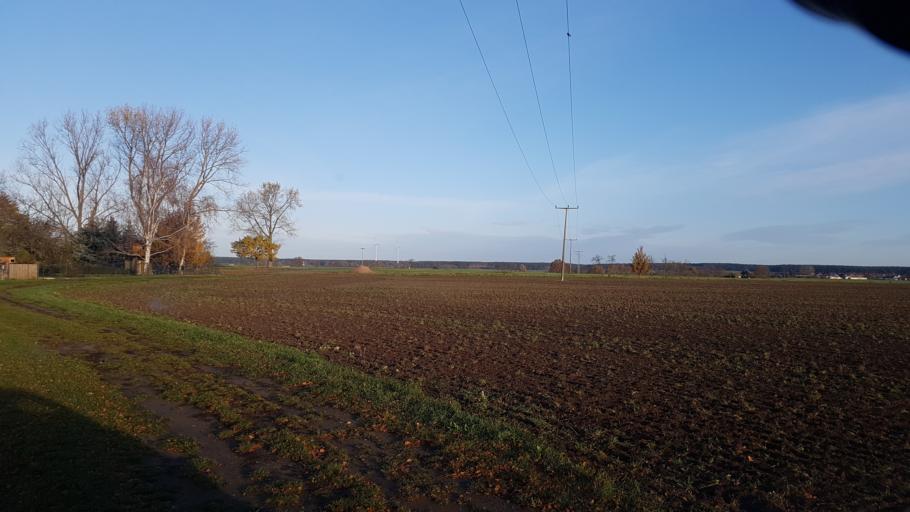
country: DE
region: Brandenburg
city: Sonnewalde
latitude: 51.6917
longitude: 13.6867
